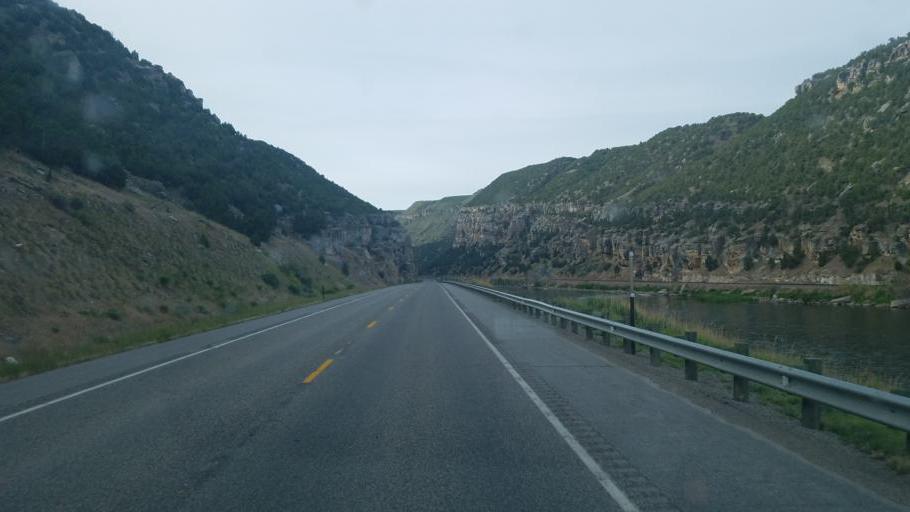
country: US
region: Wyoming
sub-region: Hot Springs County
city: Thermopolis
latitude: 43.5782
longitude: -108.2122
